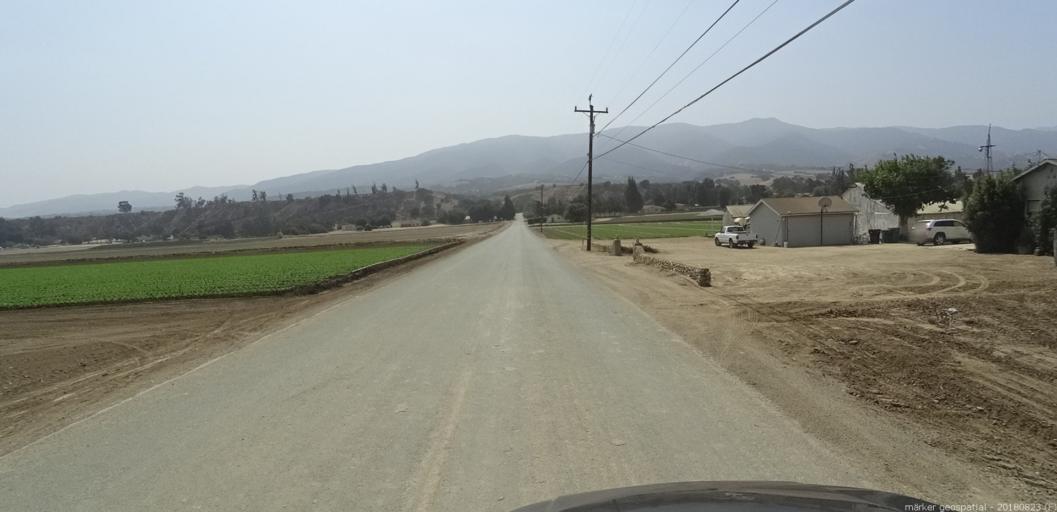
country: US
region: California
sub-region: Monterey County
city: Soledad
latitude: 36.3916
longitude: -121.3573
